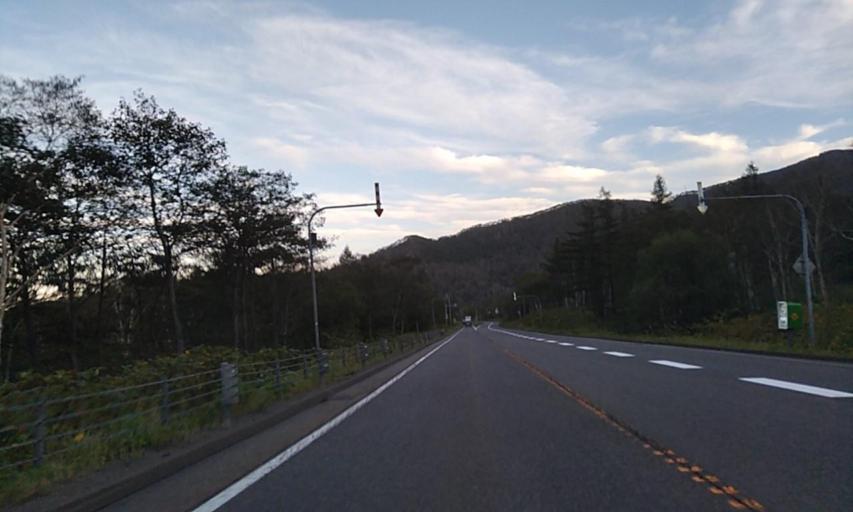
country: JP
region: Hokkaido
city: Otofuke
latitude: 42.9586
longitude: 142.7891
